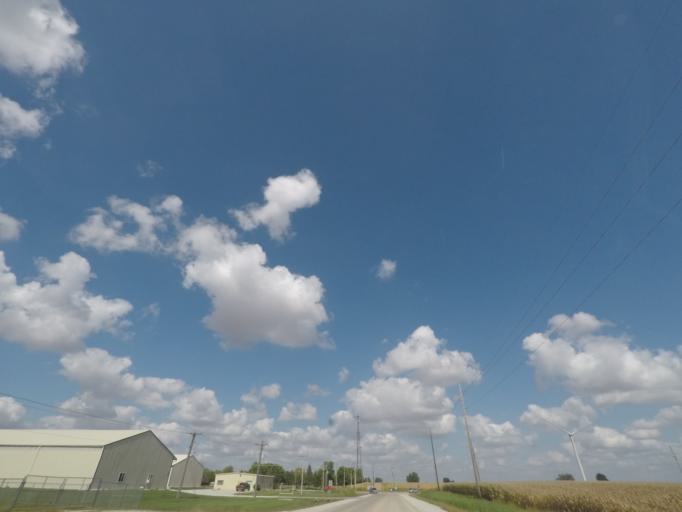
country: US
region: Iowa
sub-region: Story County
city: Nevada
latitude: 42.0212
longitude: -93.4346
